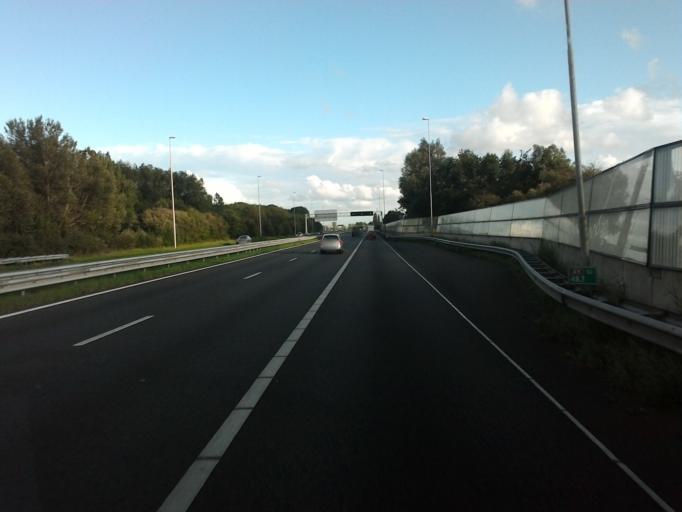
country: NL
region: North Holland
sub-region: Gemeente Velsen
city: Velsen-Zuid
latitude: 52.4317
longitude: 4.6768
